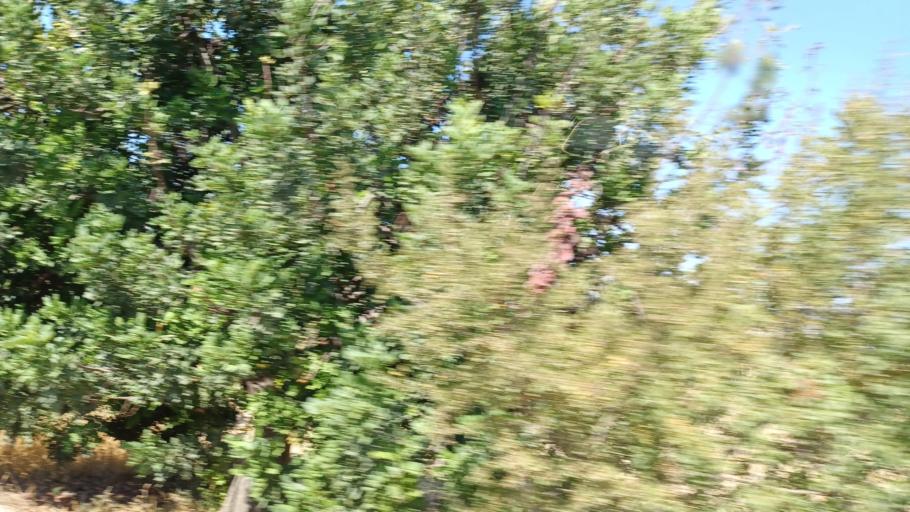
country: CY
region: Pafos
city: Polis
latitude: 34.9821
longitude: 32.4997
